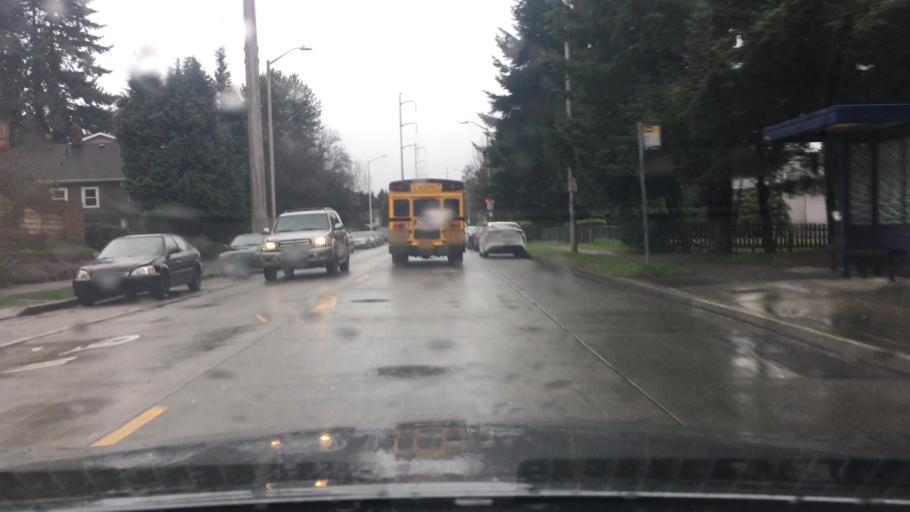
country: US
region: Washington
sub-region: King County
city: White Center
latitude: 47.5281
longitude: -122.3605
